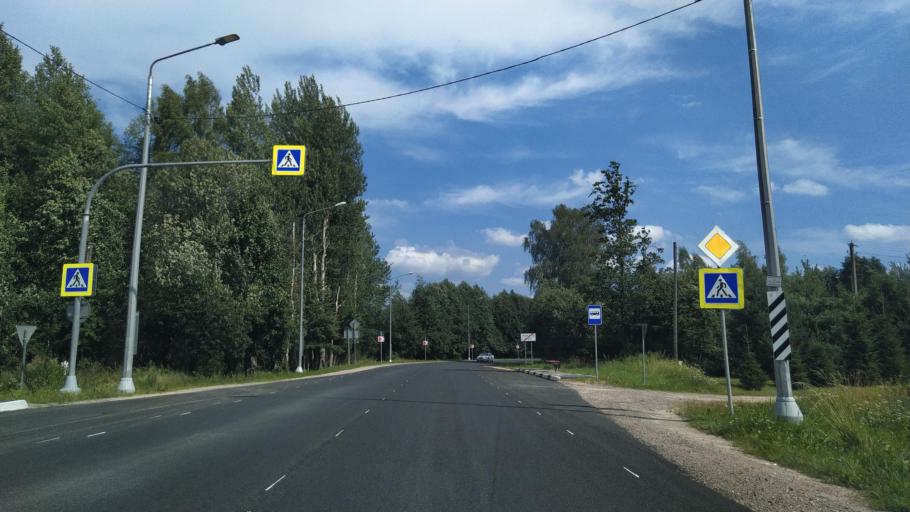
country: RU
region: Pskov
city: Porkhov
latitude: 57.7438
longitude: 29.0449
